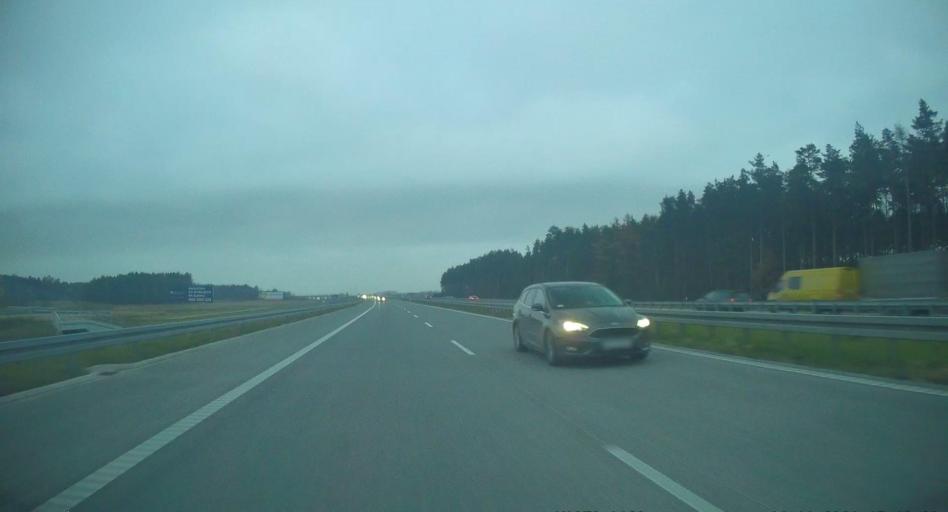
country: PL
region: Silesian Voivodeship
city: Wozniki
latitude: 50.5646
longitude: 19.0561
